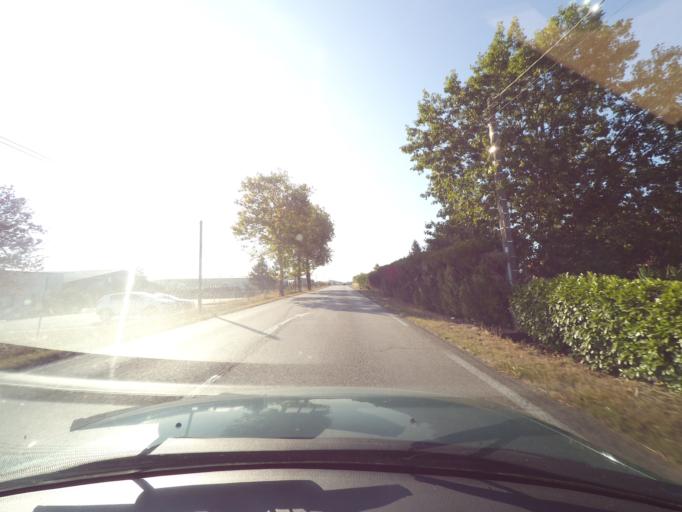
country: FR
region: Poitou-Charentes
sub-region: Departement des Deux-Sevres
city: Chiche
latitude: 46.7926
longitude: -0.3486
